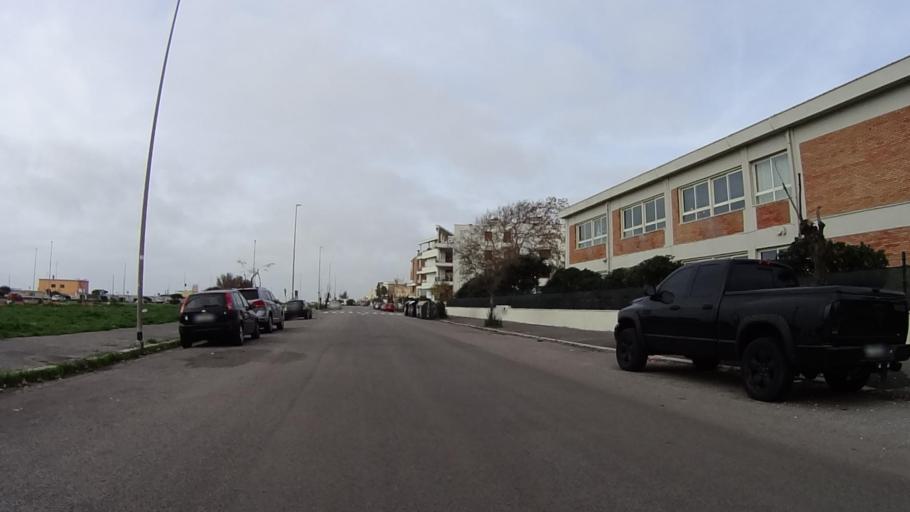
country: IT
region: Latium
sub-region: Citta metropolitana di Roma Capitale
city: Lido di Ostia
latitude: 41.7241
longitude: 12.2939
